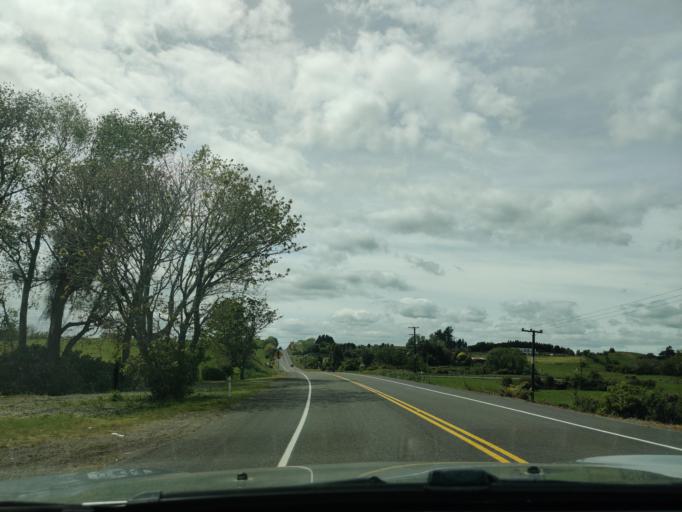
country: NZ
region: Taranaki
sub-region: New Plymouth District
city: New Plymouth
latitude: -39.1513
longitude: 174.1577
